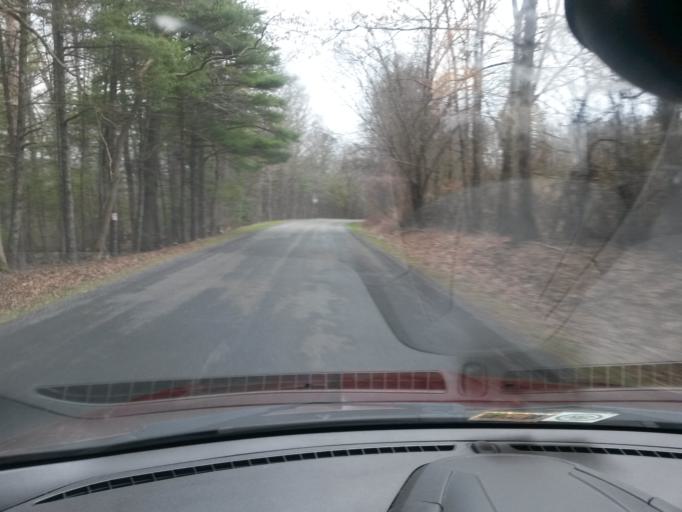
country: US
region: Virginia
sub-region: Bath County
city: Warm Springs
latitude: 38.0760
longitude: -79.8226
